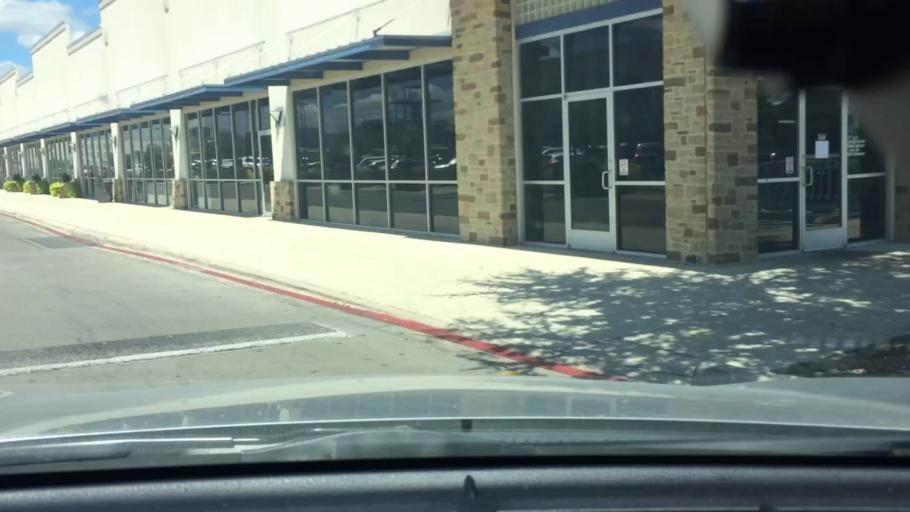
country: US
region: Texas
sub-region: Bexar County
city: Castle Hills
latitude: 29.5191
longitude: -98.5024
